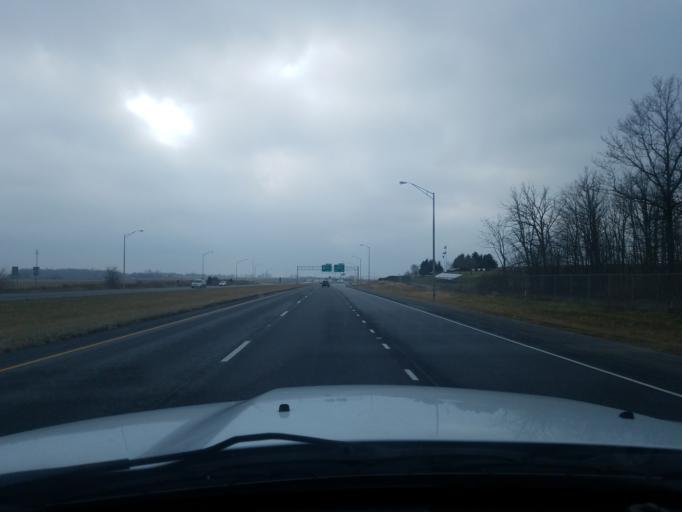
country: US
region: Indiana
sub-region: Huntington County
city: Roanoke
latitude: 40.9681
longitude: -85.2861
